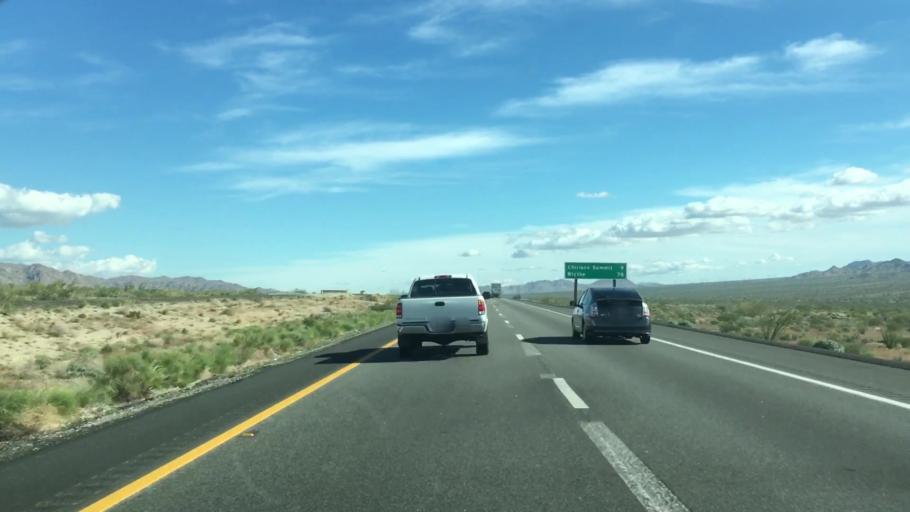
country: US
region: California
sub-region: Riverside County
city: Mecca
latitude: 33.6641
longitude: -115.8717
